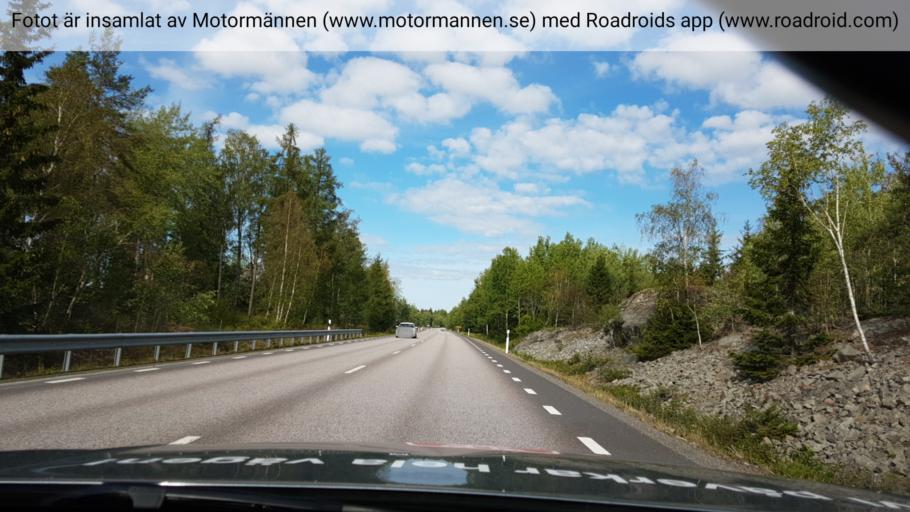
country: SE
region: Uppsala
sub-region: Osthammars Kommun
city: Bjorklinge
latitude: 59.9763
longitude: 17.3522
